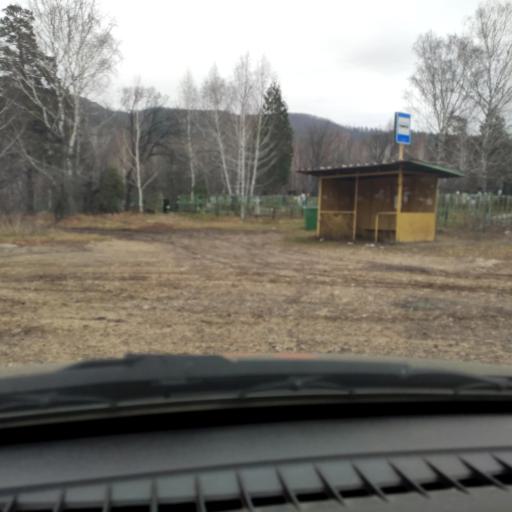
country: RU
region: Samara
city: Zhigulevsk
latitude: 53.4291
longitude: 49.6672
